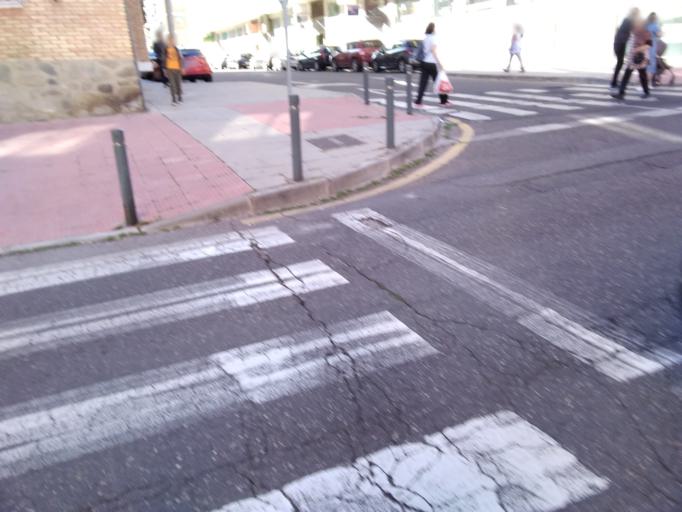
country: ES
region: Castille-La Mancha
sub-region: Province of Toledo
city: Toledo
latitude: 39.8737
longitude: -4.0344
